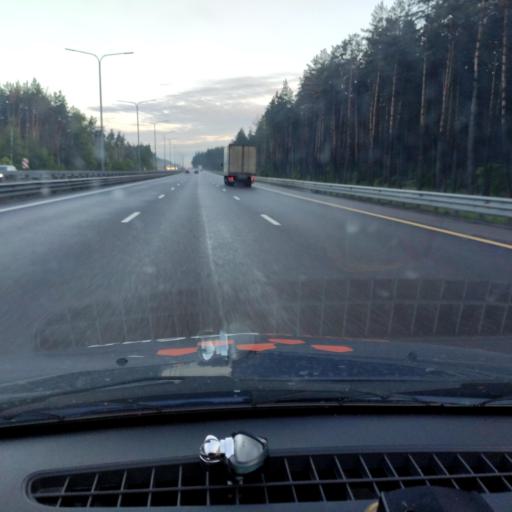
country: RU
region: Voronezj
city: Somovo
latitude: 51.7176
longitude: 39.3091
